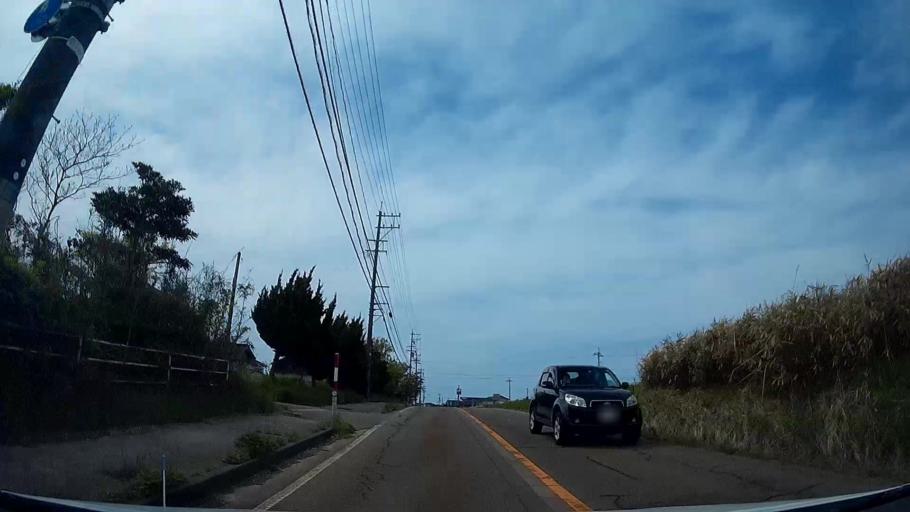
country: JP
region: Ishikawa
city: Hakui
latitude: 37.0087
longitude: 136.7650
